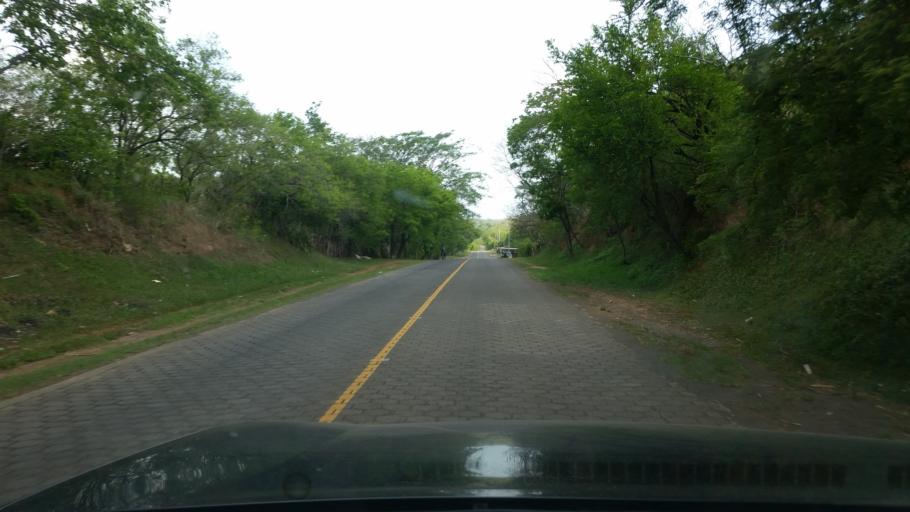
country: NI
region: Managua
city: Carlos Fonseca Amador
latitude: 12.0477
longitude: -86.5083
